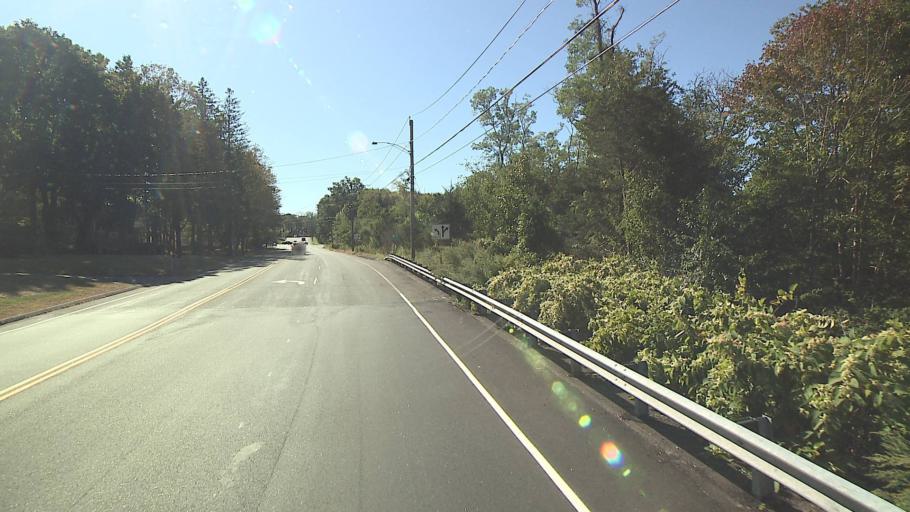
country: US
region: Connecticut
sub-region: New Haven County
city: Orange
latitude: 41.3008
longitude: -73.0180
